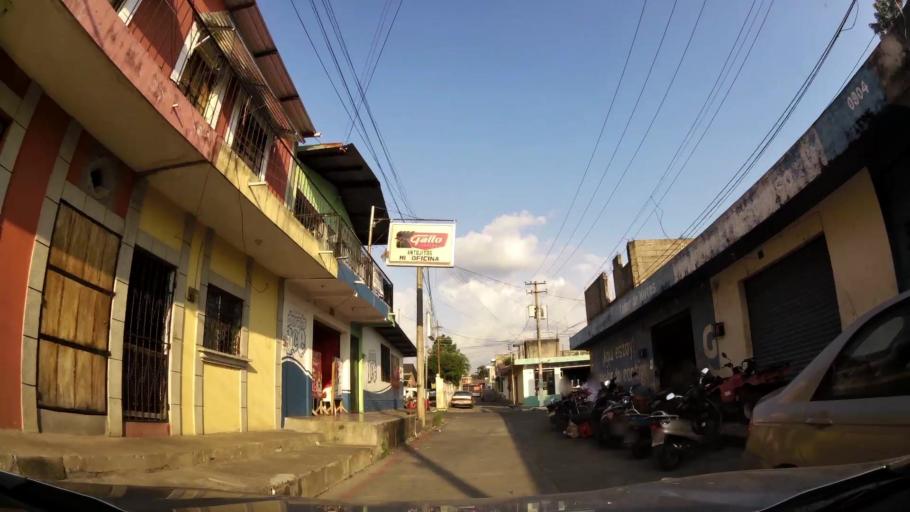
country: GT
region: Retalhuleu
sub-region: Municipio de Retalhuleu
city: Retalhuleu
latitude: 14.5354
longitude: -91.6822
